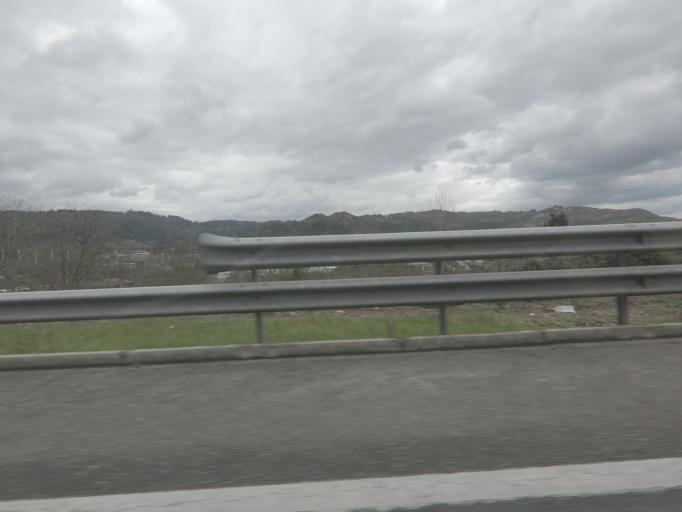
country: ES
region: Galicia
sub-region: Provincia de Ourense
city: Ourense
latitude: 42.3468
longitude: -7.9079
